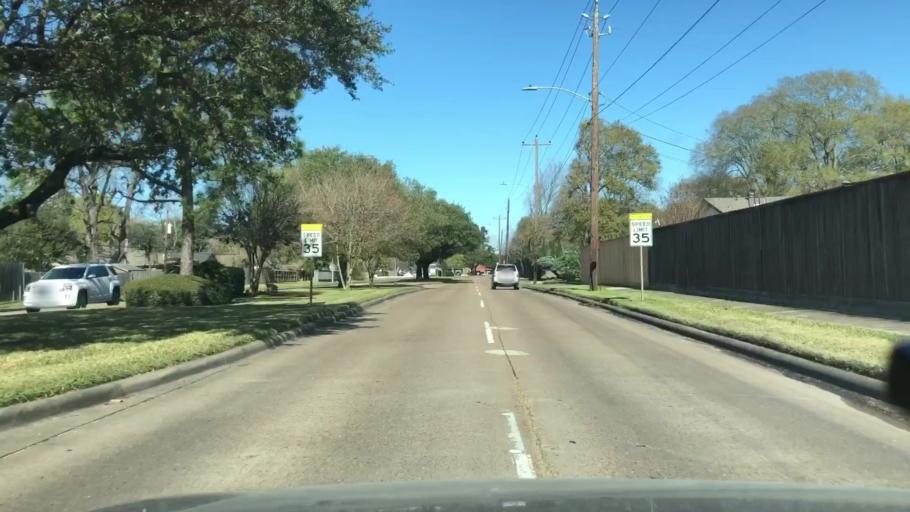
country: US
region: Texas
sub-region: Harris County
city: Bellaire
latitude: 29.6828
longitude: -95.4927
